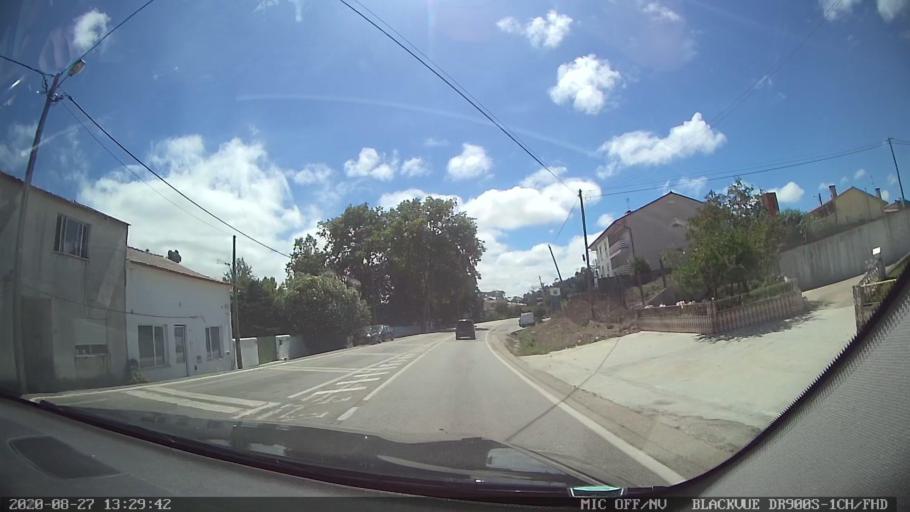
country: PT
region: Aveiro
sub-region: Vagos
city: Vagos
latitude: 40.5106
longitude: -8.6772
